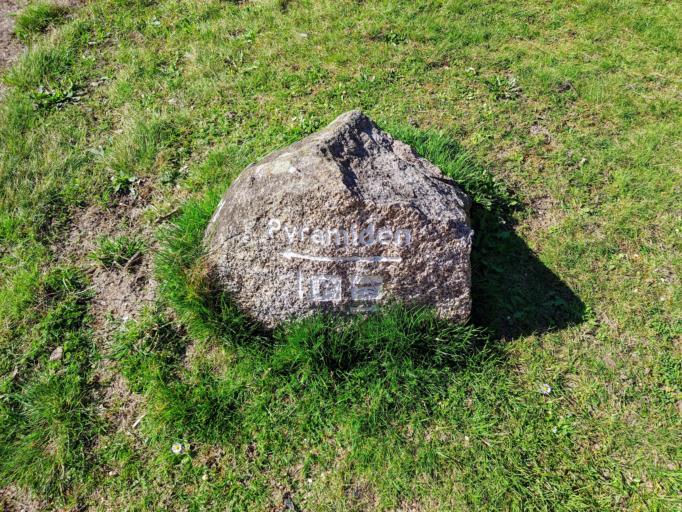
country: DE
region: Brandenburg
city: Cottbus
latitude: 51.7424
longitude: 14.3696
